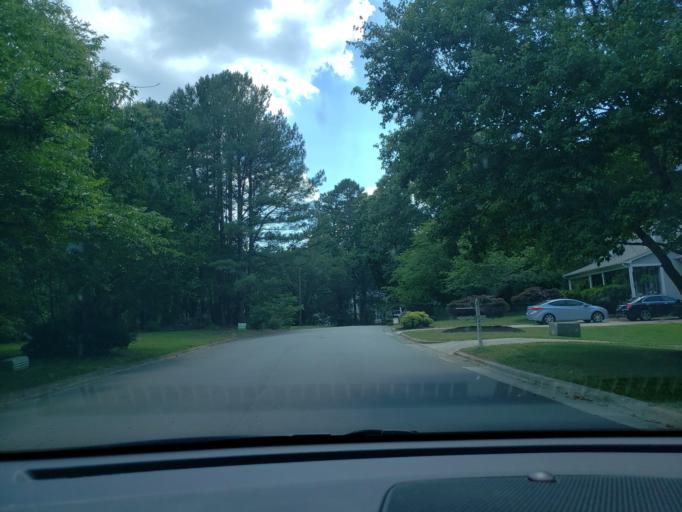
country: US
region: North Carolina
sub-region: Durham County
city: Durham
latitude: 35.9696
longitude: -78.9788
